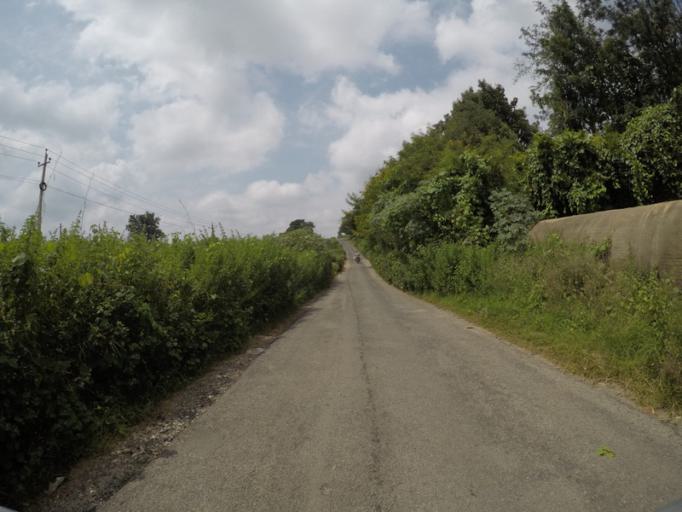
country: IN
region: Karnataka
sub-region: Bangalore Urban
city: Bangalore
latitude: 12.8624
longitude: 77.5249
